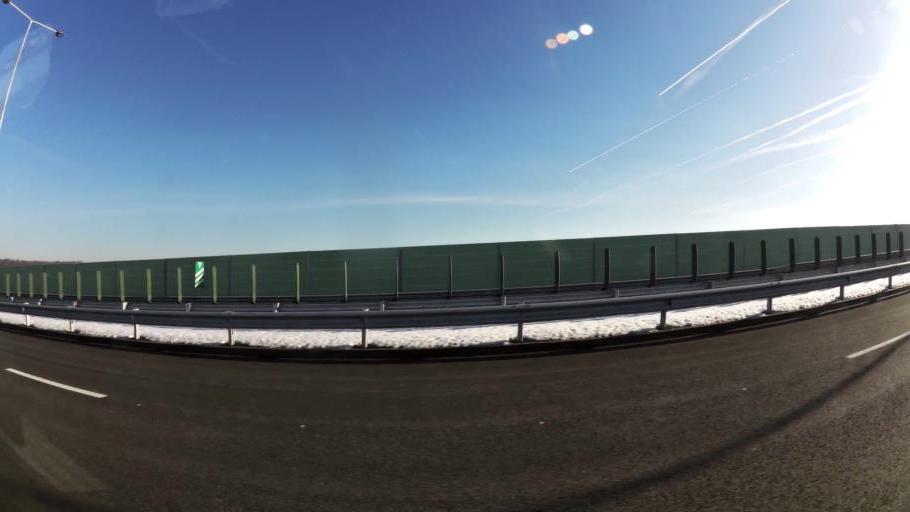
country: RO
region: Ilfov
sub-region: Voluntari City
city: Voluntari
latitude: 44.4860
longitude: 26.1420
